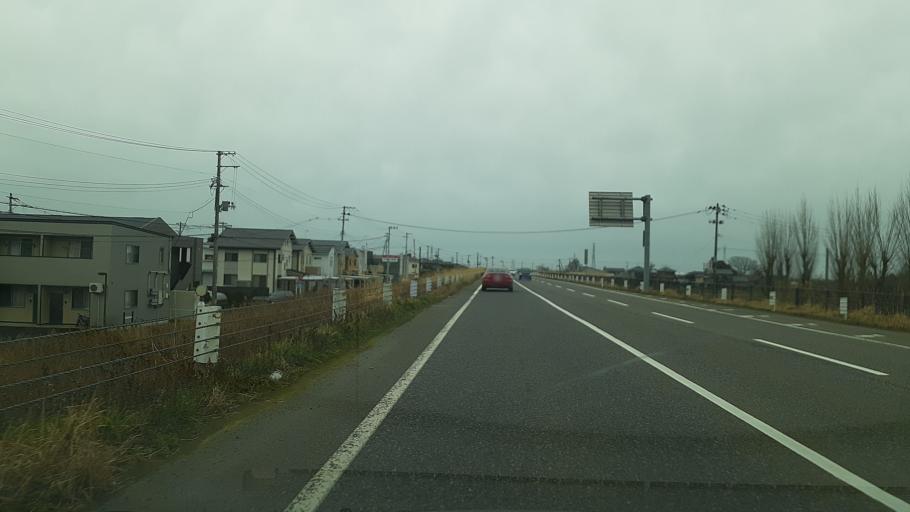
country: JP
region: Niigata
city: Niitsu-honcho
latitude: 37.7962
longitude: 139.1076
